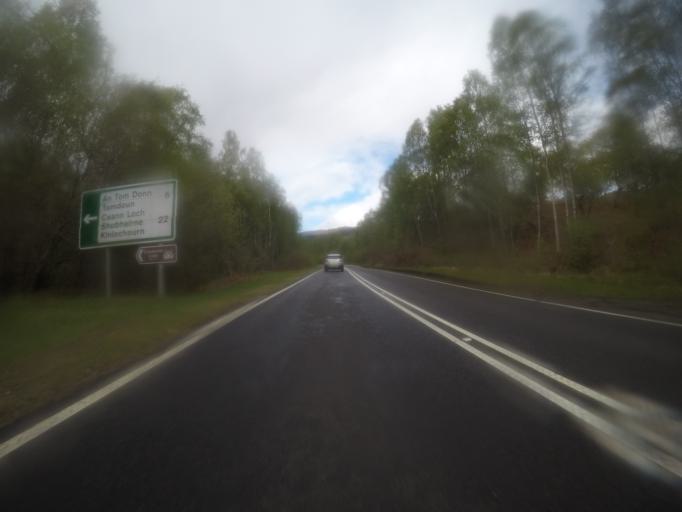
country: GB
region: Scotland
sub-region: Highland
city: Spean Bridge
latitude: 57.0825
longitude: -4.8986
